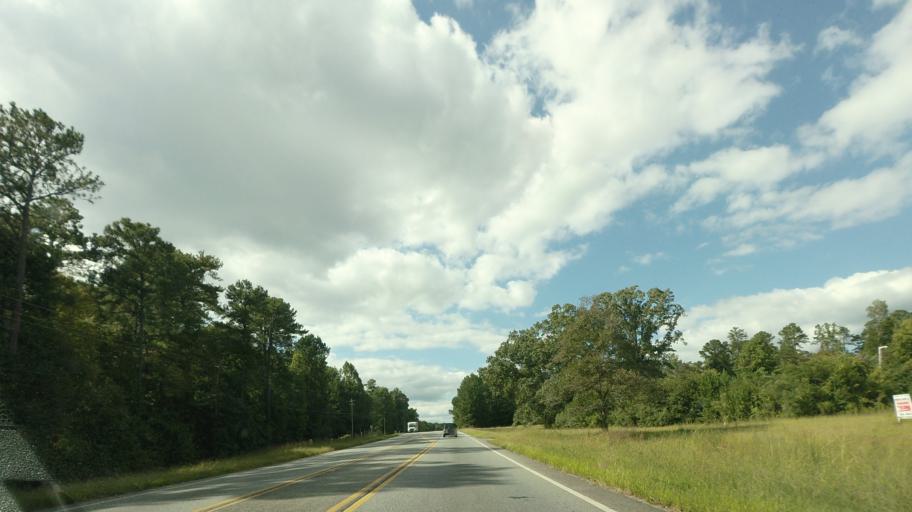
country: US
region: Georgia
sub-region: Bibb County
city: Macon
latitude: 32.9413
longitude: -83.7205
